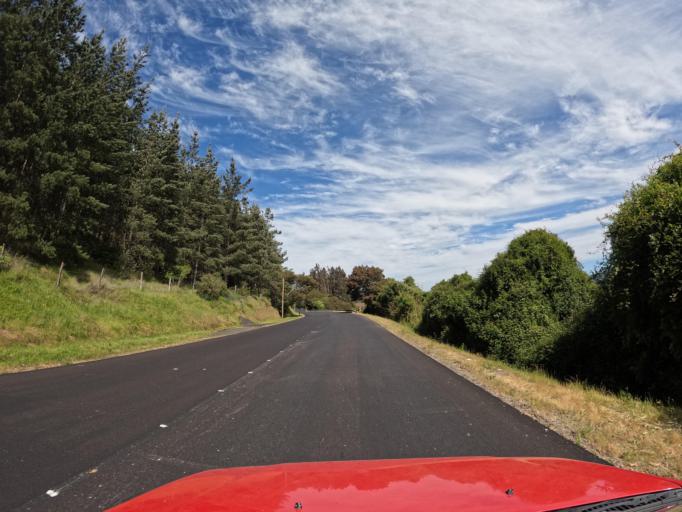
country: CL
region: Maule
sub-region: Provincia de Talca
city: Constitucion
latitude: -35.0473
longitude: -72.0494
